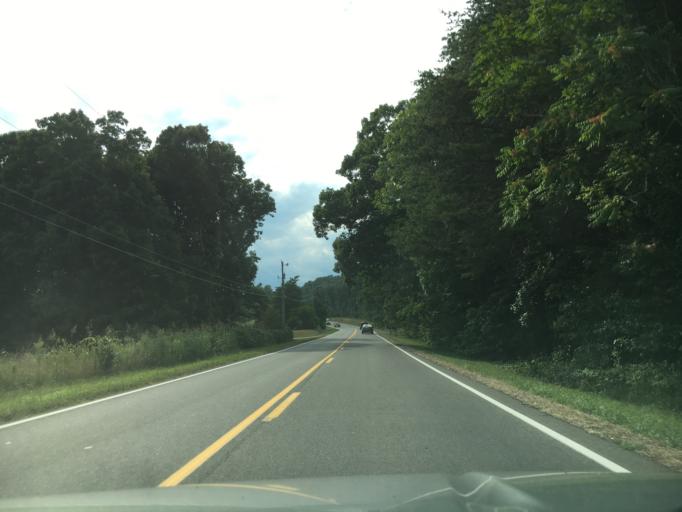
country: US
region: Virginia
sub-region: Campbell County
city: Rustburg
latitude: 37.2719
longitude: -79.1533
